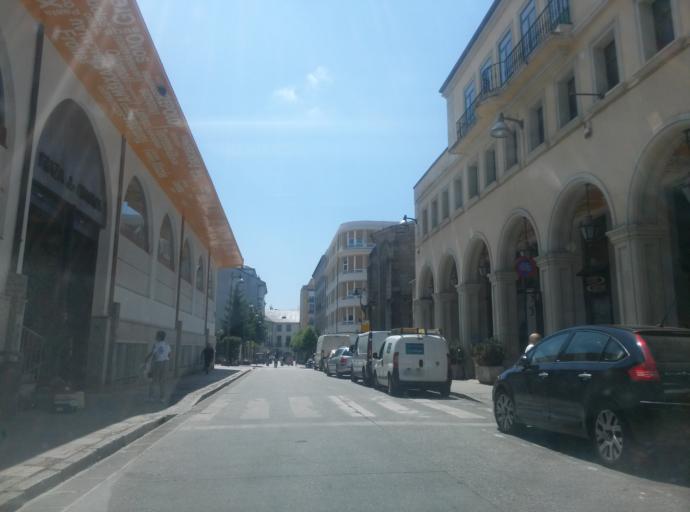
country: ES
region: Galicia
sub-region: Provincia de Lugo
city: Lugo
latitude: 43.0120
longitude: -7.5583
